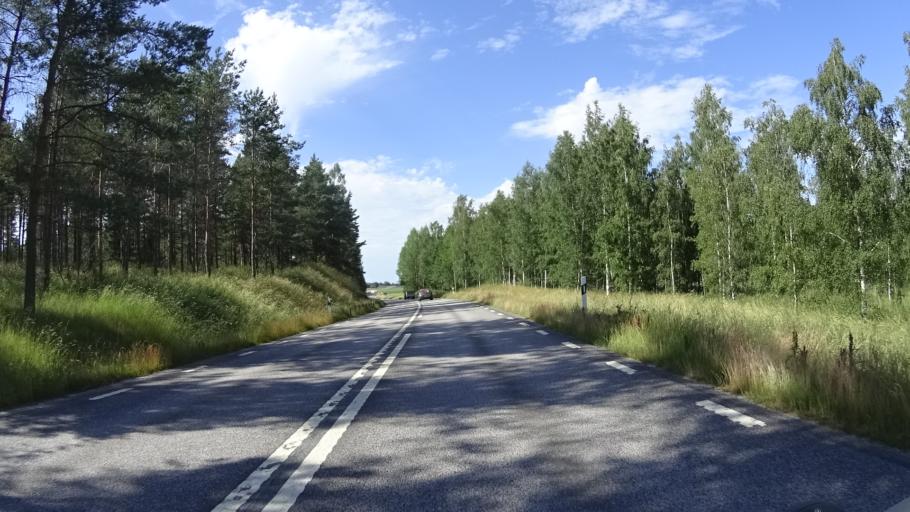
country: SE
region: OEstergoetland
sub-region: Linkopings Kommun
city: Sturefors
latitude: 58.3251
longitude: 15.8600
